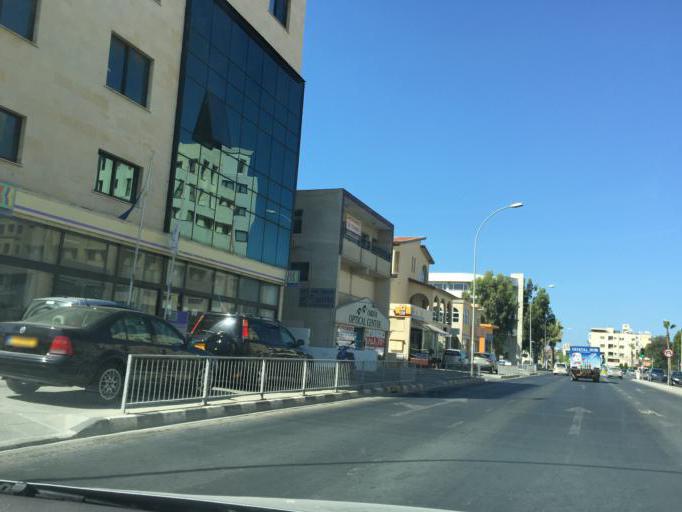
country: CY
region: Limassol
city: Limassol
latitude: 34.6676
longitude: 33.0259
